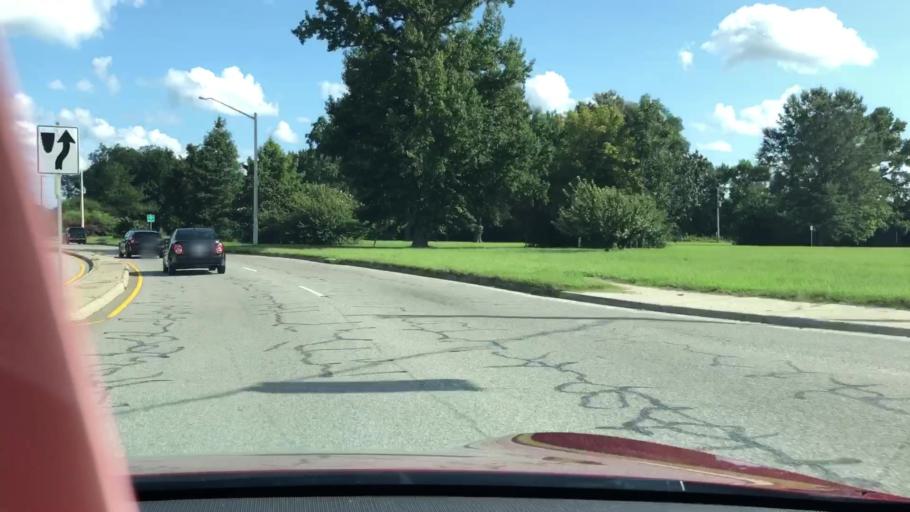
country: US
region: Virginia
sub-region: City of Virginia Beach
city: Virginia Beach
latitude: 36.8403
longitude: -76.0212
